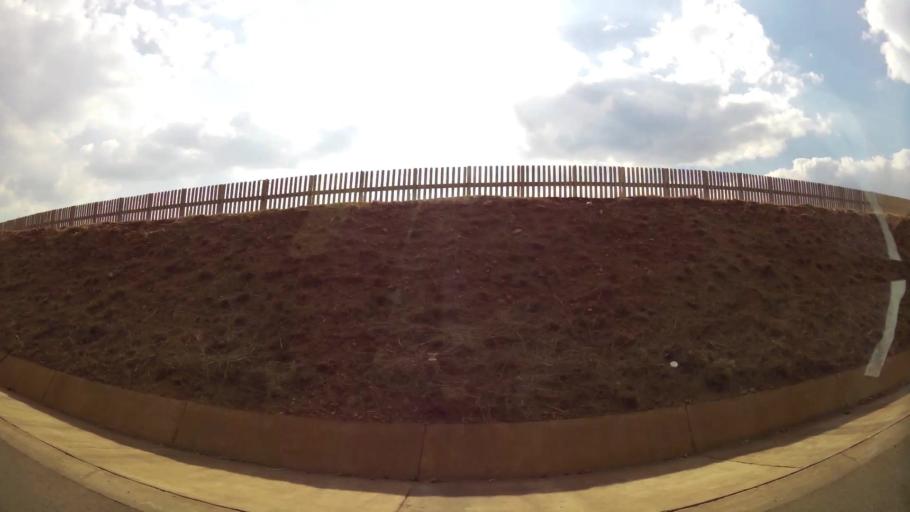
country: ZA
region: Gauteng
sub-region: Ekurhuleni Metropolitan Municipality
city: Tembisa
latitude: -25.9285
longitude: 28.2158
